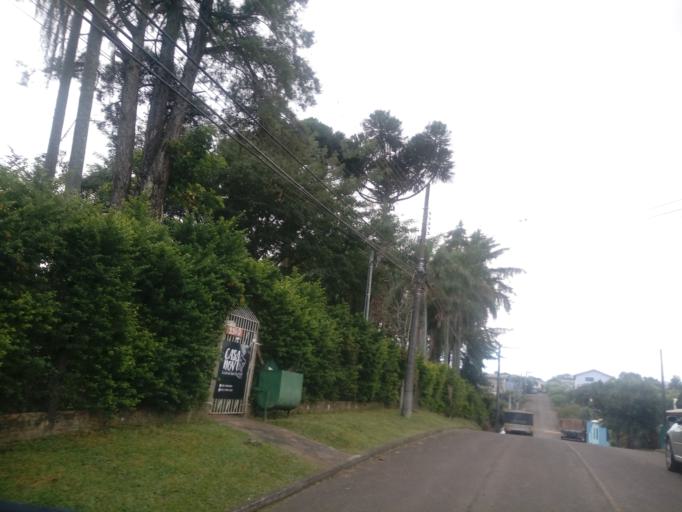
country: BR
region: Santa Catarina
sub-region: Chapeco
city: Chapeco
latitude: -27.1152
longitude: -52.6269
